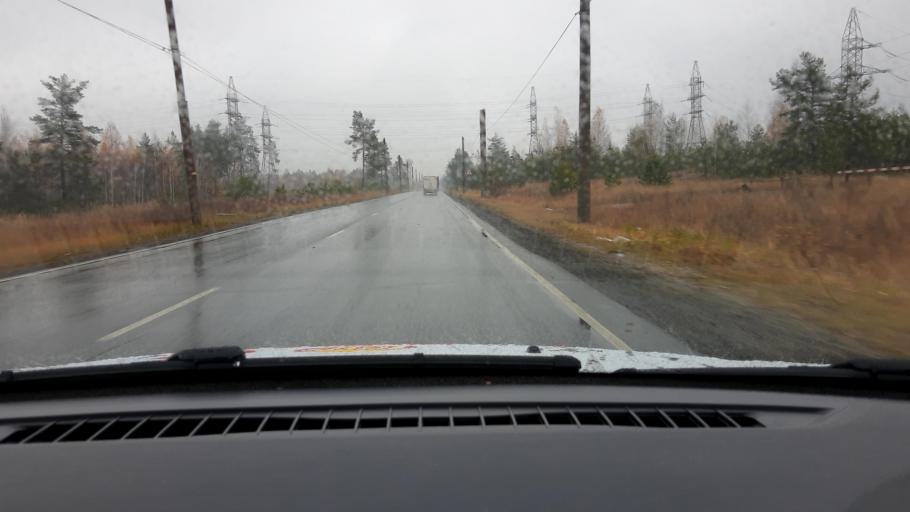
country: RU
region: Nizjnij Novgorod
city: Dzerzhinsk
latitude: 56.2663
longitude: 43.5322
